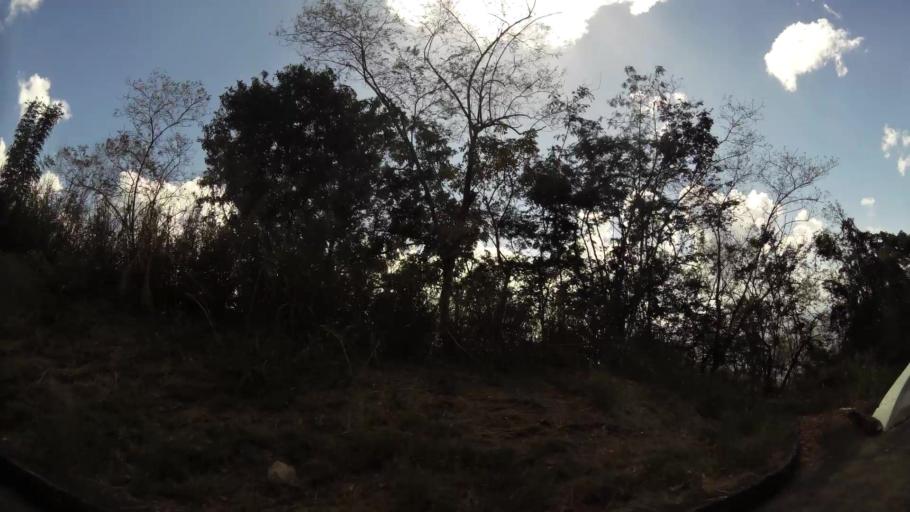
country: MQ
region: Martinique
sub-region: Martinique
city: Saint-Pierre
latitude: 14.6936
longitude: -61.1713
